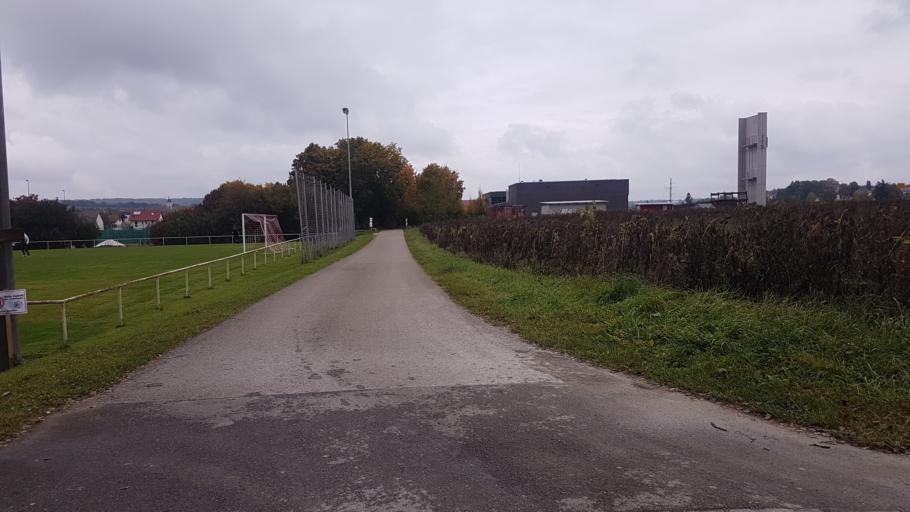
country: DE
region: Baden-Wuerttemberg
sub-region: Tuebingen Region
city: Dusslingen
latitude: 48.4424
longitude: 9.0565
